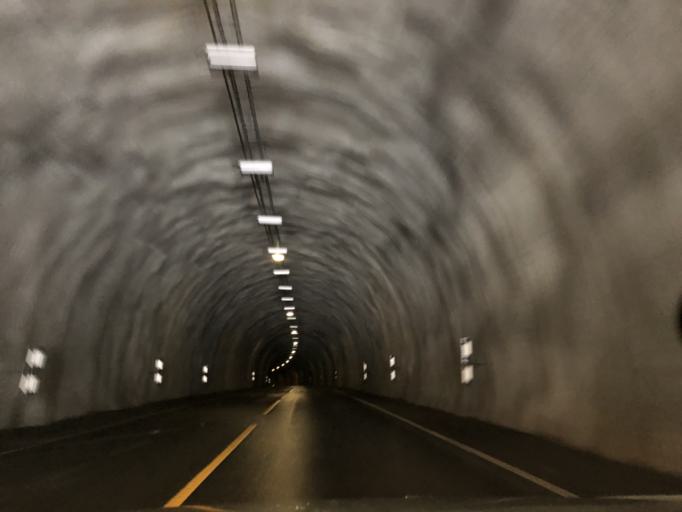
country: NO
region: Rogaland
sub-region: Sauda
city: Sauda
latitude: 59.5299
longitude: 6.5955
